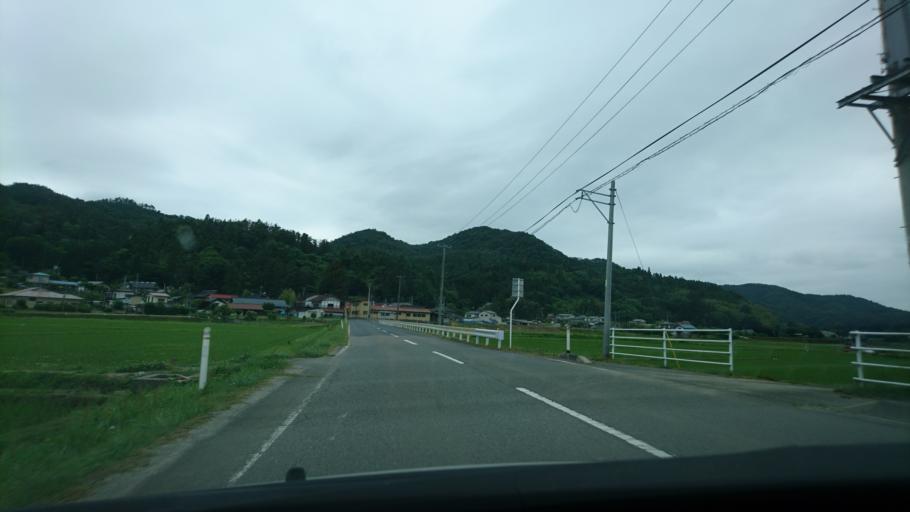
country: JP
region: Iwate
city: Ichinoseki
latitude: 38.9634
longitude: 141.2426
